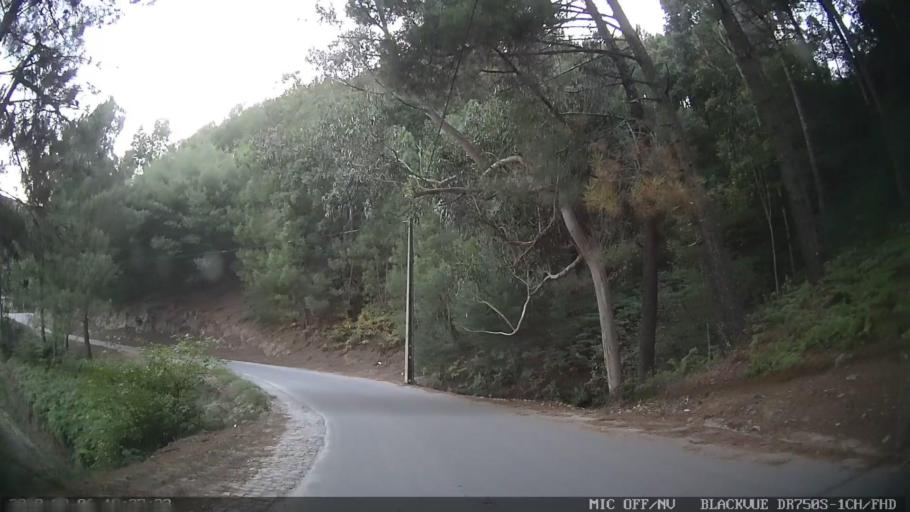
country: PT
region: Vila Real
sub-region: Mesao Frio
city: Mesao Frio
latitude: 41.1811
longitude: -7.9103
